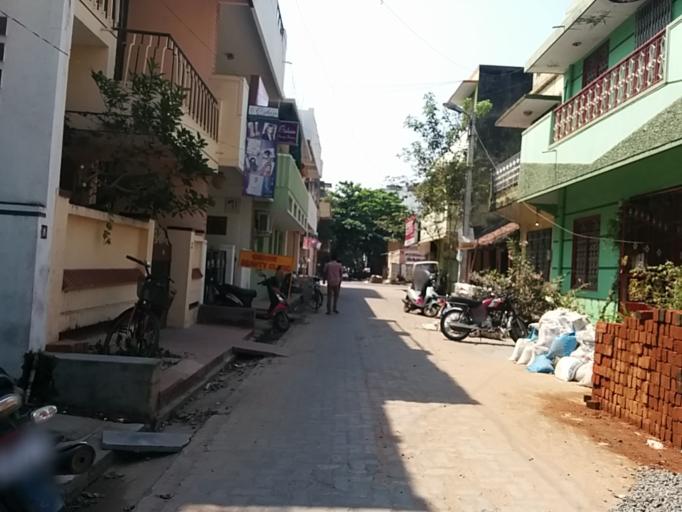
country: IN
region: Pondicherry
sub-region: Puducherry
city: Puducherry
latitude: 11.9351
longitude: 79.8316
